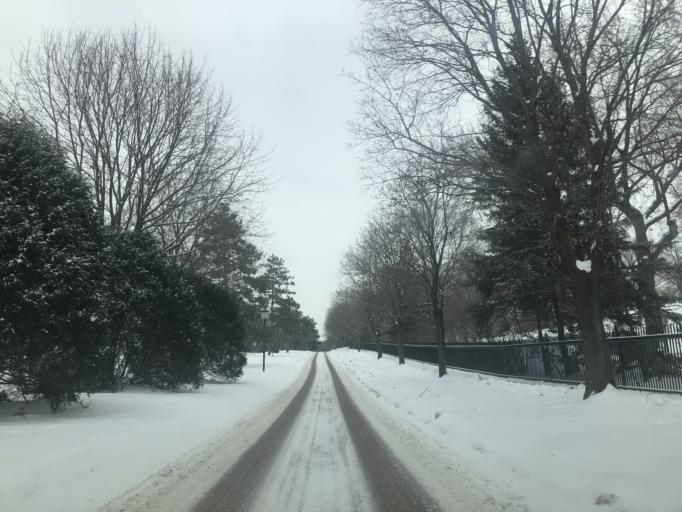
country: US
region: Minnesota
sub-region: Hennepin County
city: Richfield
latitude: 44.9317
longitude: -93.2934
